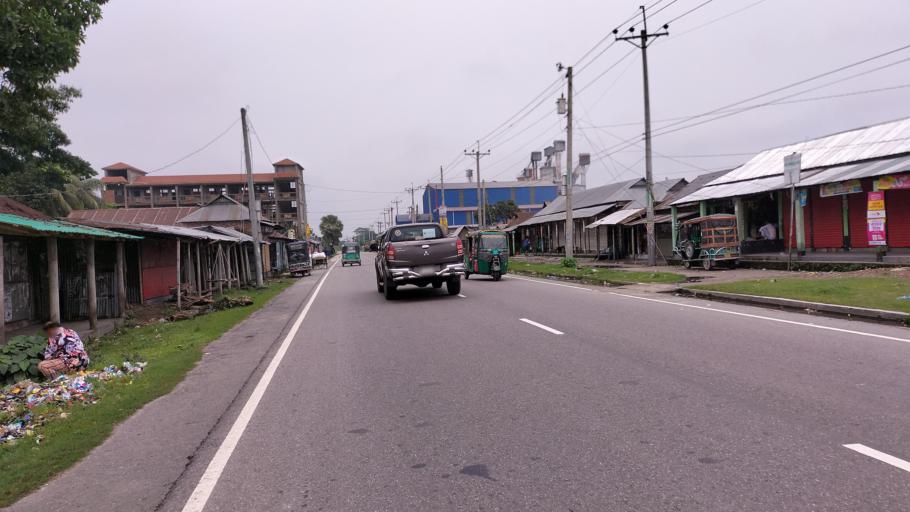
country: BD
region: Dhaka
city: Netrakona
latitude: 24.8511
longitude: 90.6268
